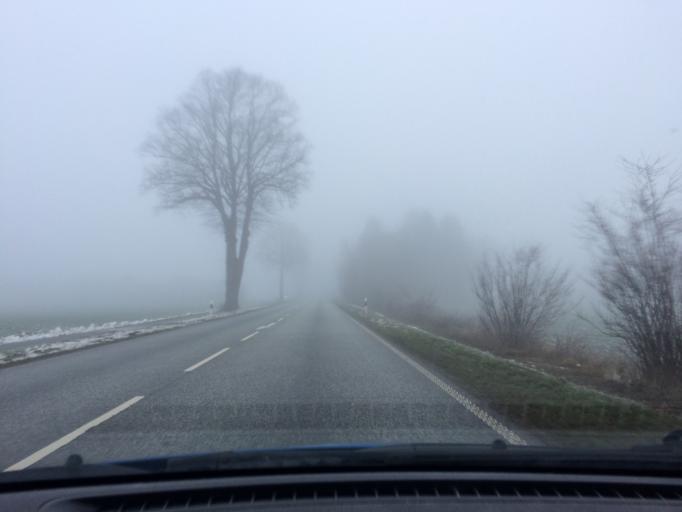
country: DE
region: Schleswig-Holstein
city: Grabau
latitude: 53.5222
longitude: 10.5056
